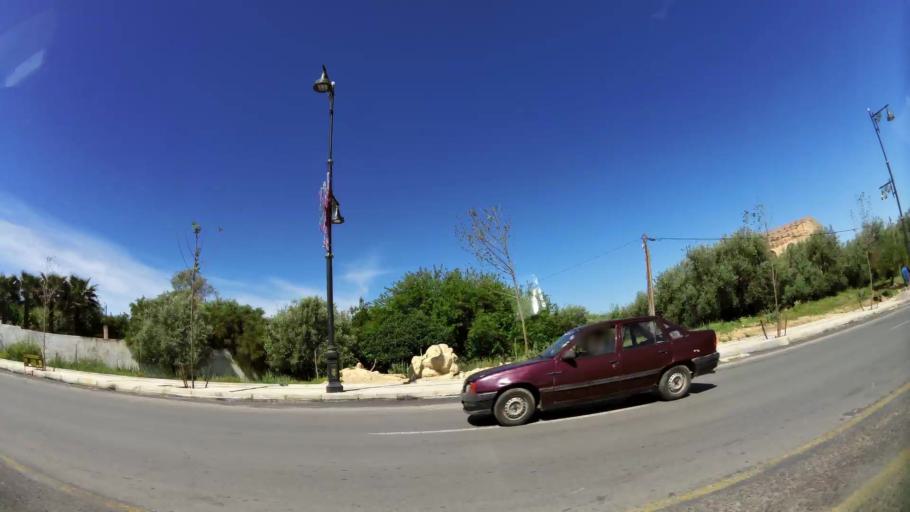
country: MA
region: Meknes-Tafilalet
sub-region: Meknes
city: Meknes
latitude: 33.8688
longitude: -5.5388
